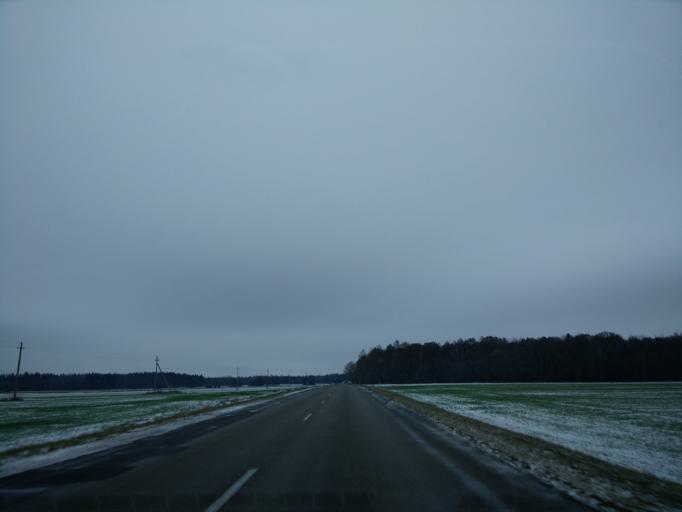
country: LT
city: Ariogala
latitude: 55.3959
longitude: 23.3401
